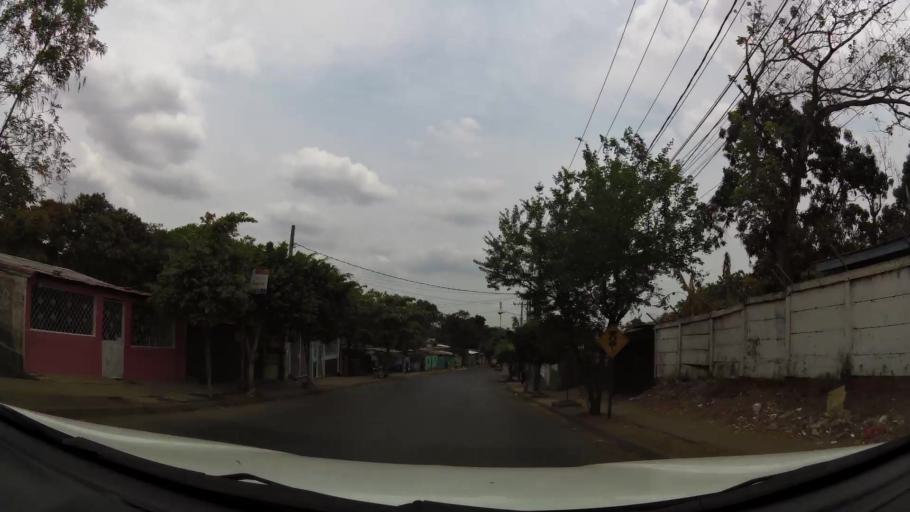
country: NI
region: Managua
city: Managua
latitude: 12.1104
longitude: -86.2329
